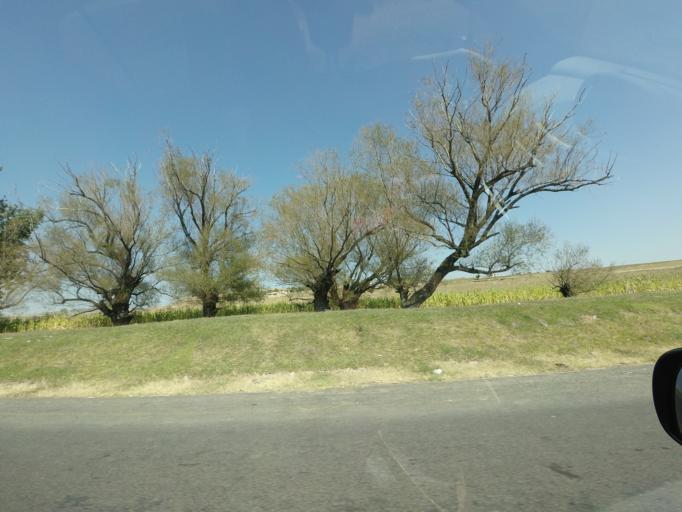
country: LS
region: Leribe
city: Leribe
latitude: -29.0101
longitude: 27.9983
